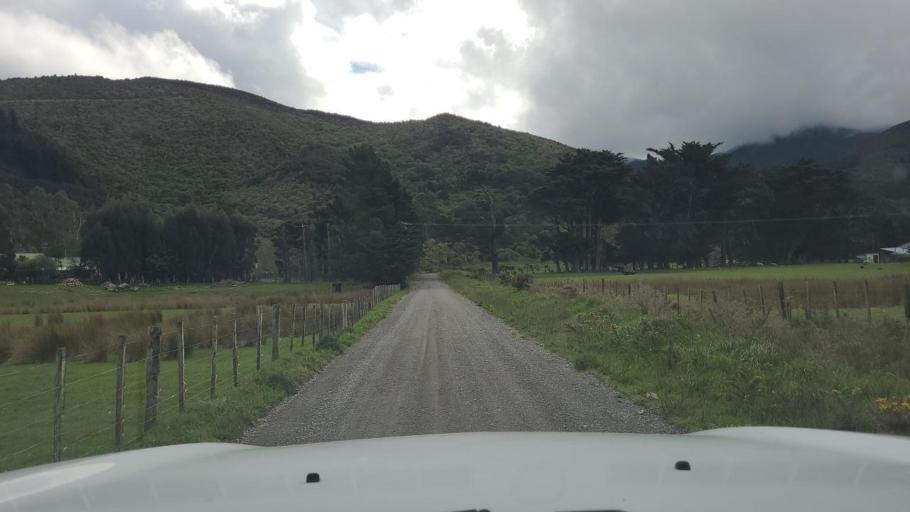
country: NZ
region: Wellington
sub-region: Upper Hutt City
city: Upper Hutt
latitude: -41.1695
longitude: 175.2406
